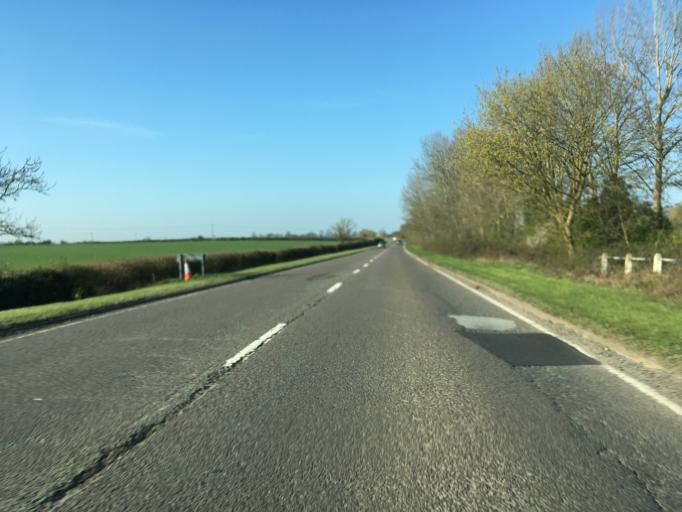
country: GB
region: England
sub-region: Northamptonshire
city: Deanshanger
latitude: 52.0362
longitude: -0.8967
